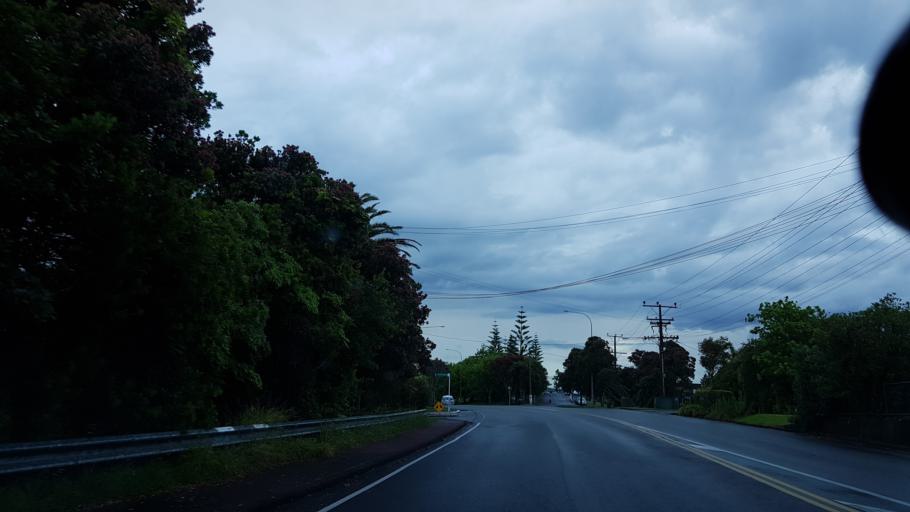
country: NZ
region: Auckland
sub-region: Auckland
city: North Shore
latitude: -36.7889
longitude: 174.7208
